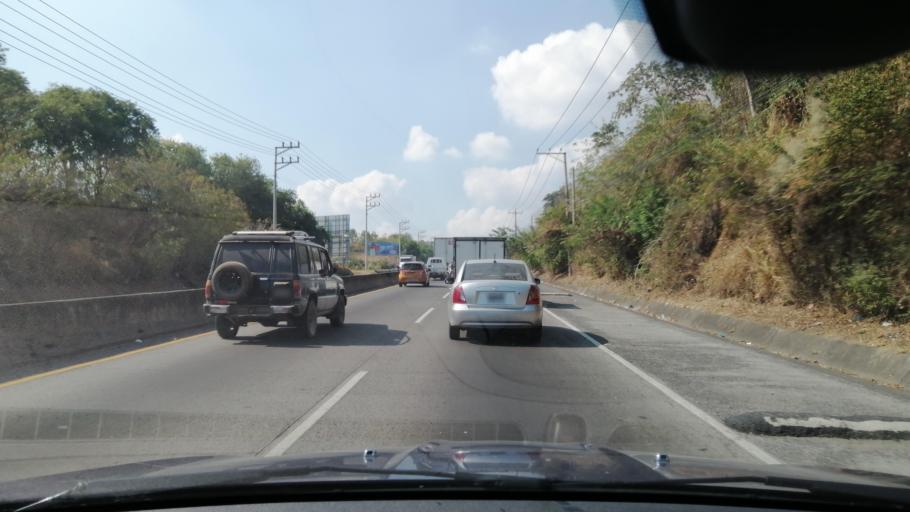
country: SV
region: San Salvador
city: Ayutuxtepeque
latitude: 13.7533
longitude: -89.2171
